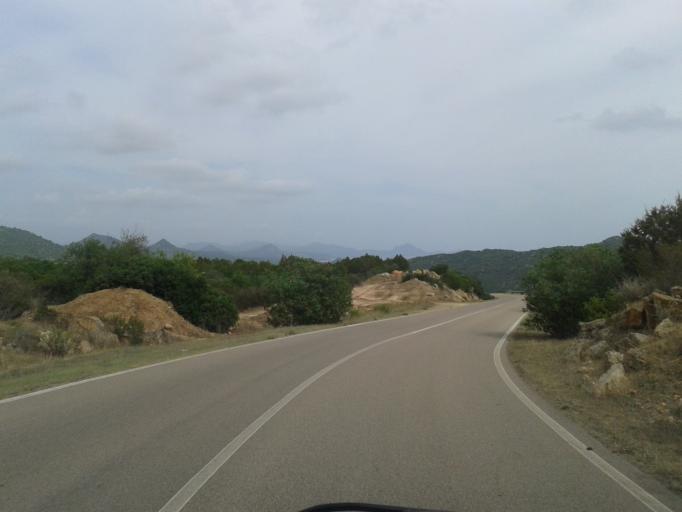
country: IT
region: Sardinia
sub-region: Provincia di Cagliari
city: Villasimius
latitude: 39.1681
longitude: 9.5607
